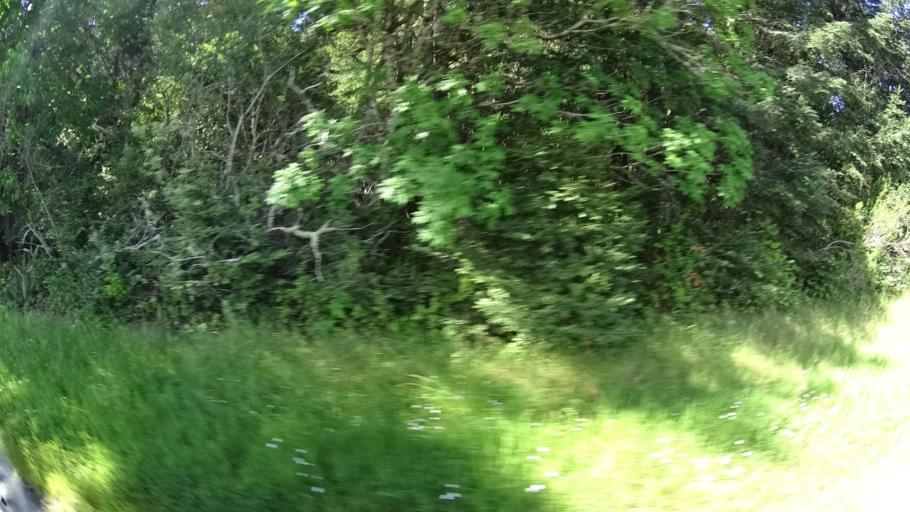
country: US
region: California
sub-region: Humboldt County
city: Ferndale
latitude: 40.3422
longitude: -124.3199
